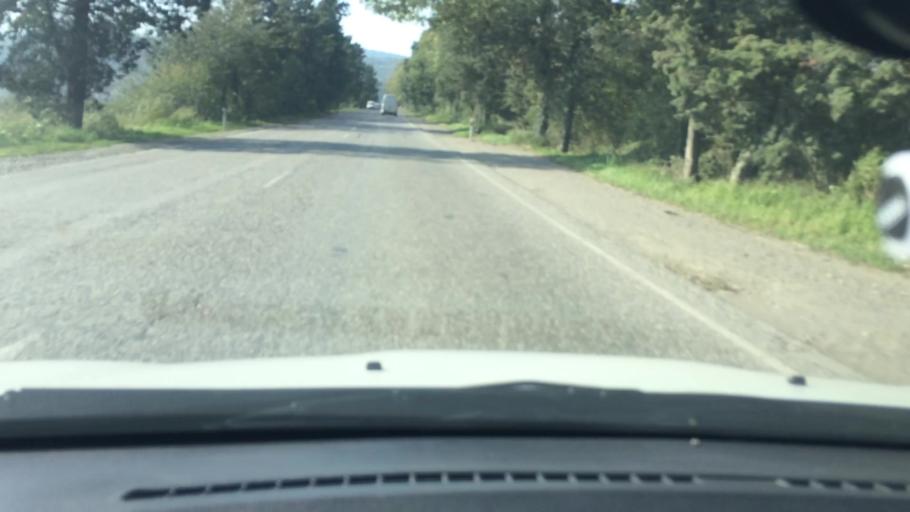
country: GE
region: Imereti
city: Samtredia
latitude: 42.1234
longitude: 42.3336
